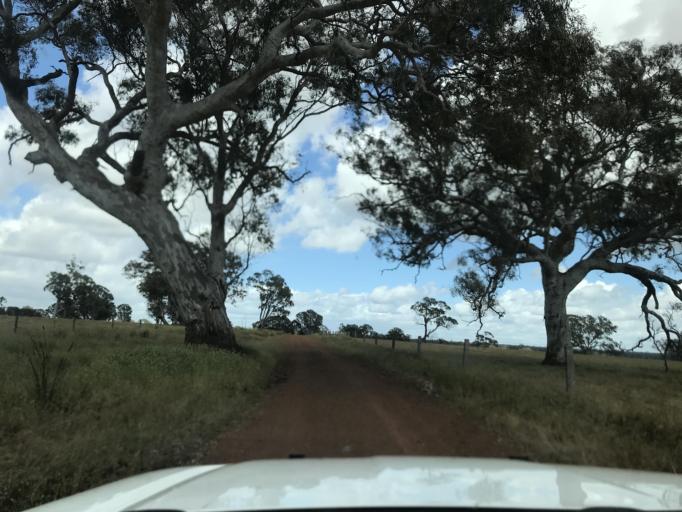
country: AU
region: South Australia
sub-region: Wattle Range
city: Penola
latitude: -37.1937
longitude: 141.4221
